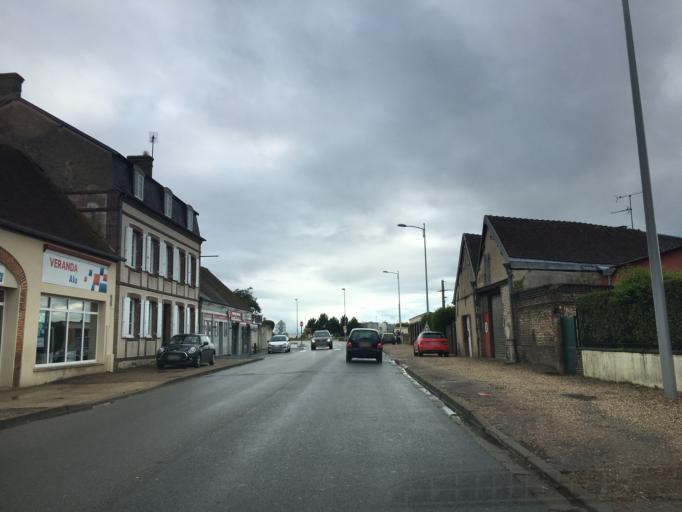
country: FR
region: Haute-Normandie
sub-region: Departement de l'Eure
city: Verneuil-sur-Avre
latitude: 48.7356
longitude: 0.9211
